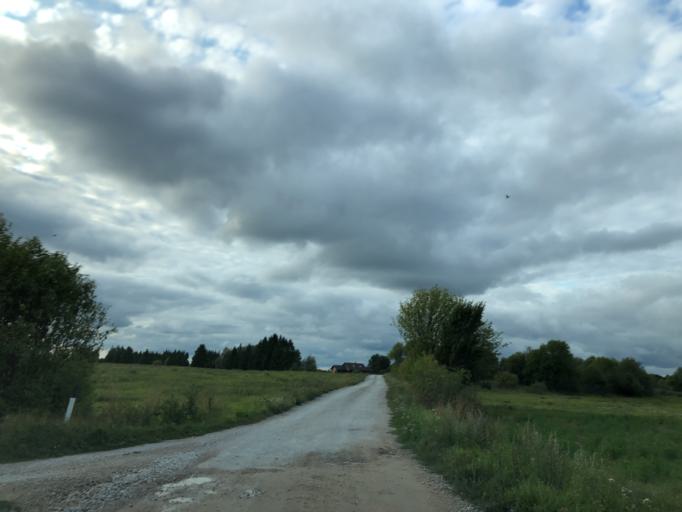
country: EE
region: Hiiumaa
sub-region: Kaerdla linn
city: Kardla
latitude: 58.7835
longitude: 22.7864
